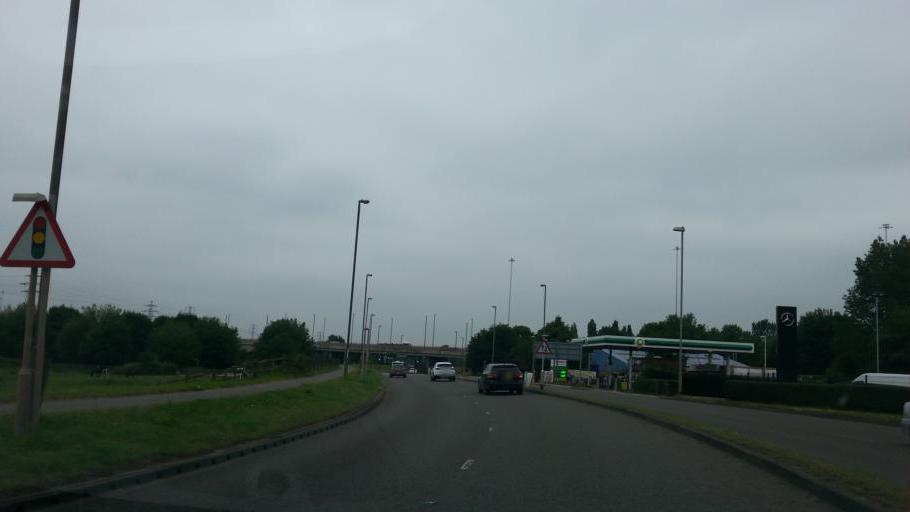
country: GB
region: England
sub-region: Nottinghamshire
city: Ruddington
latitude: 52.9218
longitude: -1.1664
